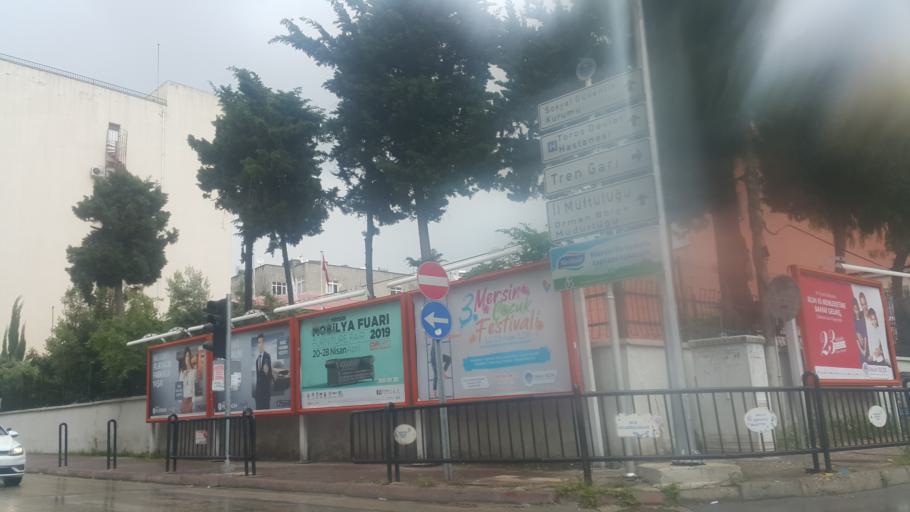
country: TR
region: Mersin
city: Mercin
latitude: 36.8038
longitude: 34.6313
